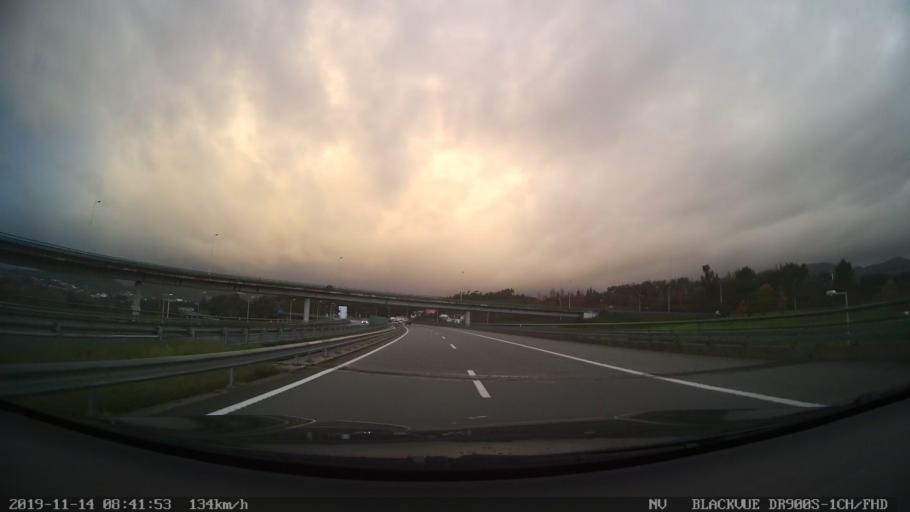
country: PT
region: Viana do Castelo
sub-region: Ponte de Lima
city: Ponte de Lima
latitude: 41.7771
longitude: -8.5601
